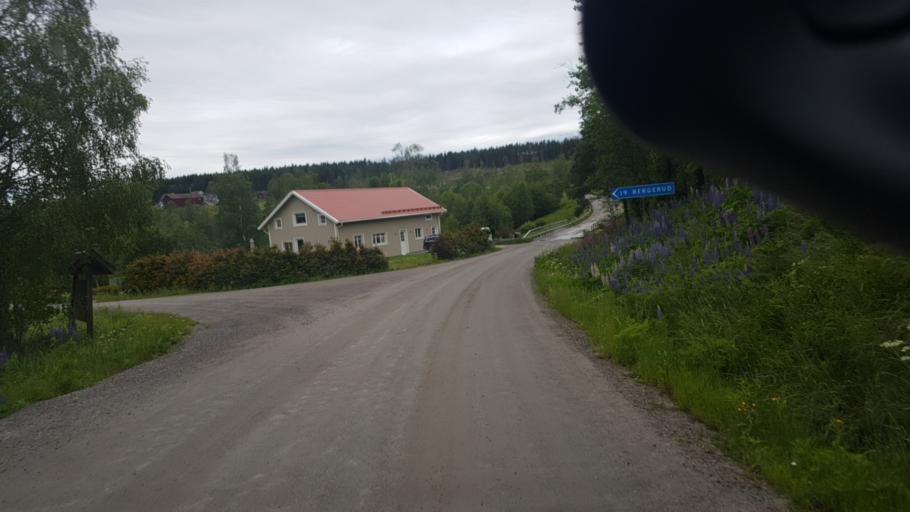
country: NO
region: Ostfold
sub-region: Romskog
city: Romskog
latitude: 59.6687
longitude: 11.9316
